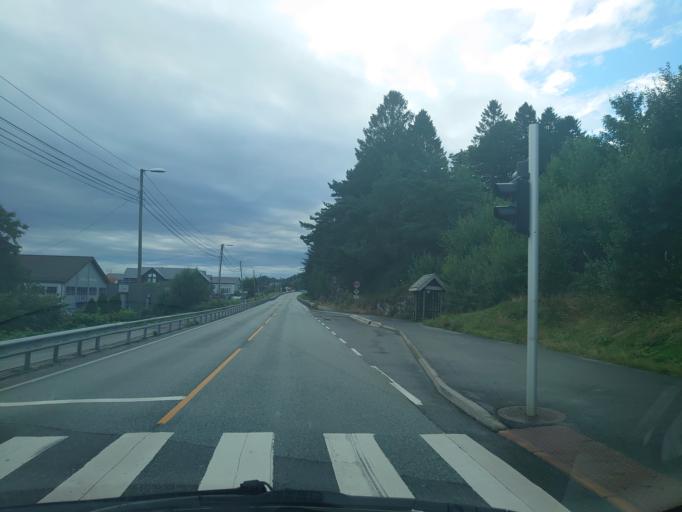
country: NO
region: Hordaland
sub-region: Lindas
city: Isdalsto
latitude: 60.5599
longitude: 5.2565
